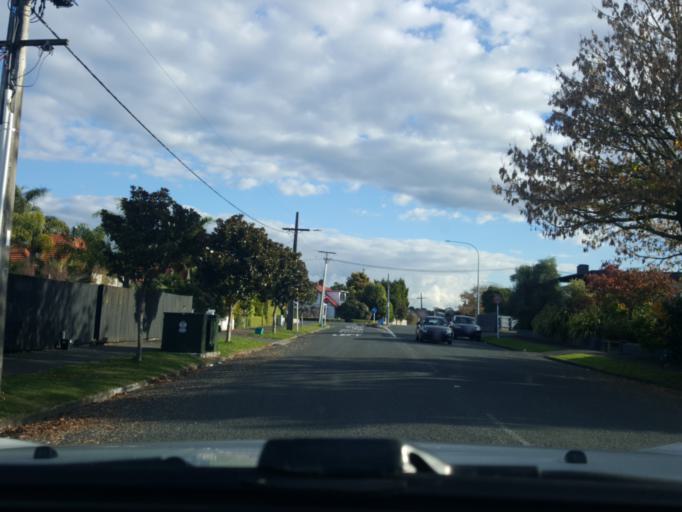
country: NZ
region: Waikato
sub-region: Hamilton City
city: Hamilton
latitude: -37.7716
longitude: 175.2647
